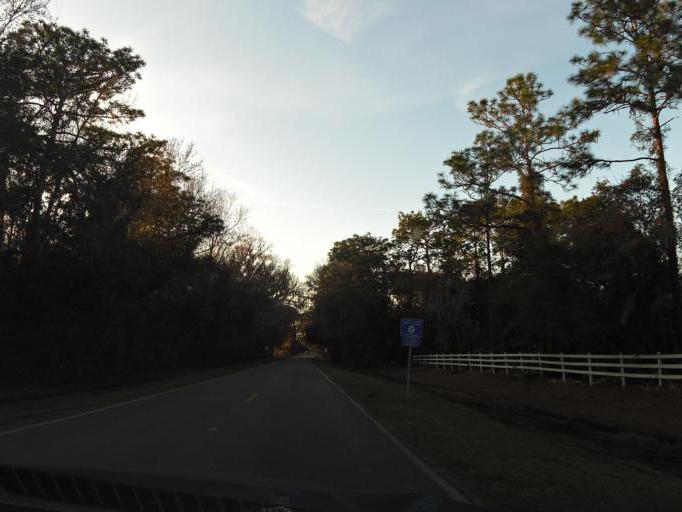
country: US
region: Florida
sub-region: Clay County
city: Green Cove Springs
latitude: 29.9012
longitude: -81.5847
